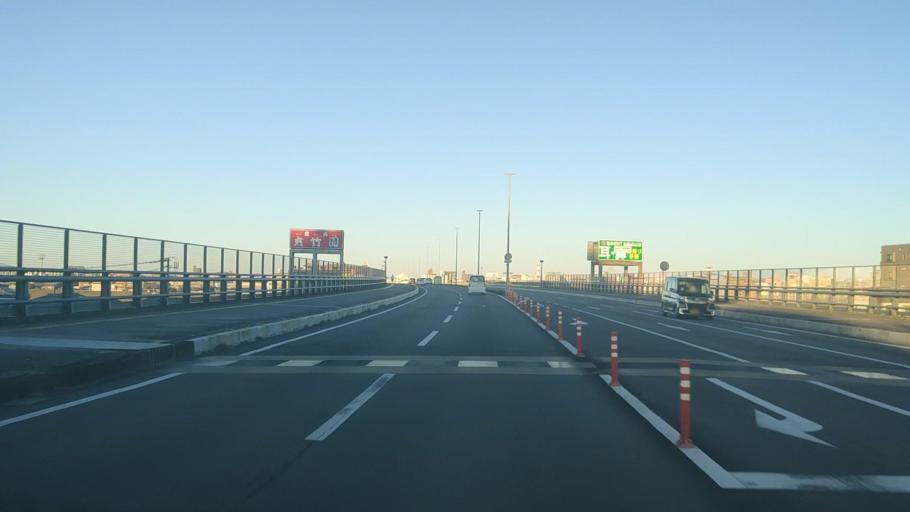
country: JP
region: Miyazaki
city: Miyazaki-shi
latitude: 31.9055
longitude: 131.4091
